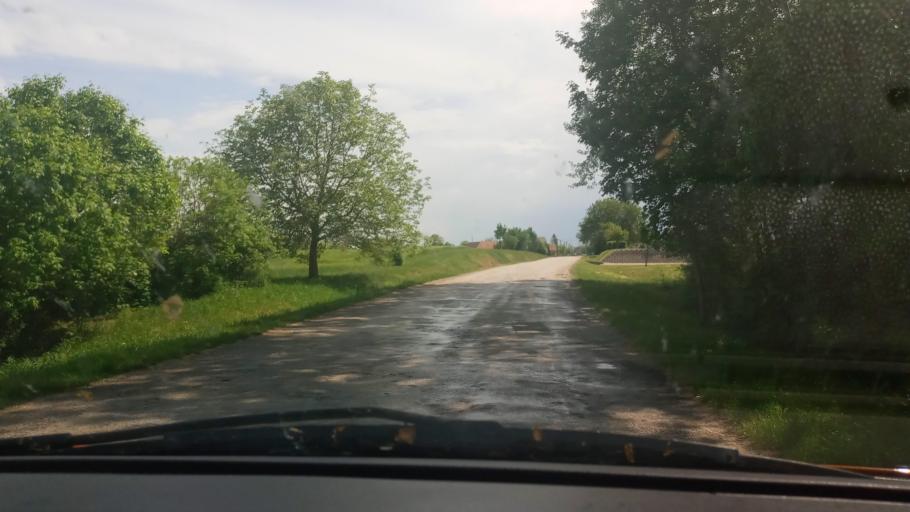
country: HU
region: Baranya
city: Siklos
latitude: 45.7966
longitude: 18.3499
